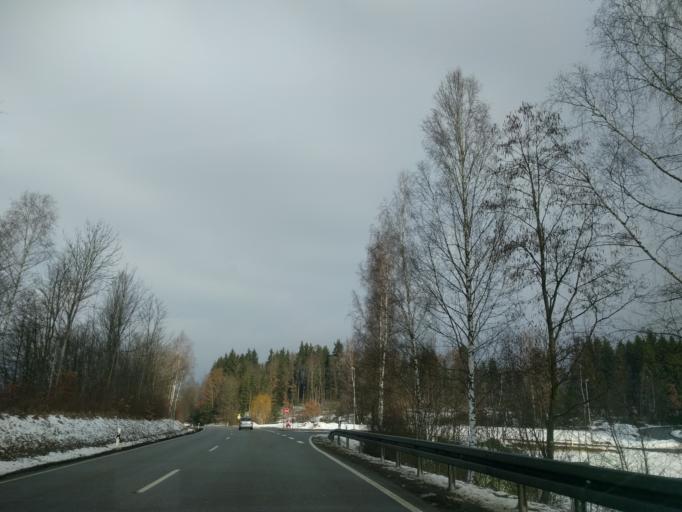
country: DE
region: Bavaria
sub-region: Lower Bavaria
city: Zwiesel
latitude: 49.0243
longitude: 13.2467
